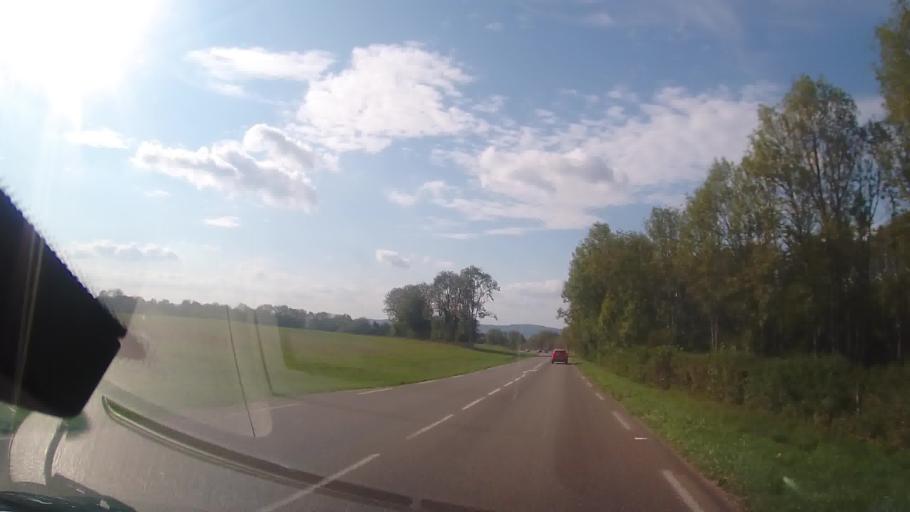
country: FR
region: Franche-Comte
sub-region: Departement du Jura
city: Clairvaux-les-Lacs
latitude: 46.5823
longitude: 5.7709
